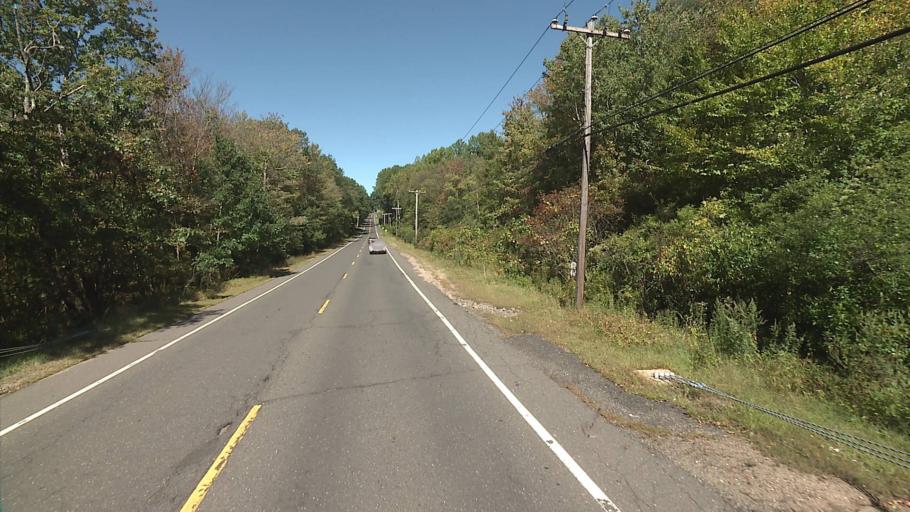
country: US
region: Connecticut
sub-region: New Haven County
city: Prospect
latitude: 41.4864
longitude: -72.9725
